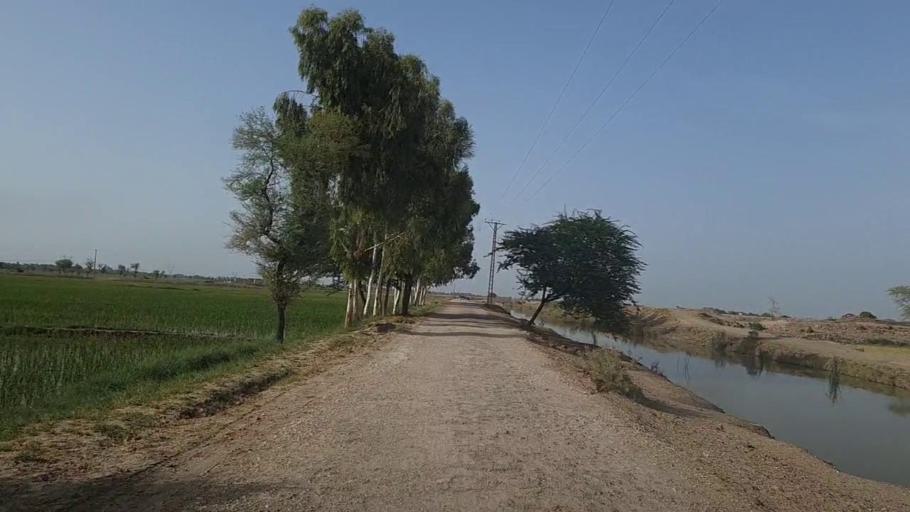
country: PK
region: Sindh
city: Sita Road
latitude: 27.1093
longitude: 67.8760
